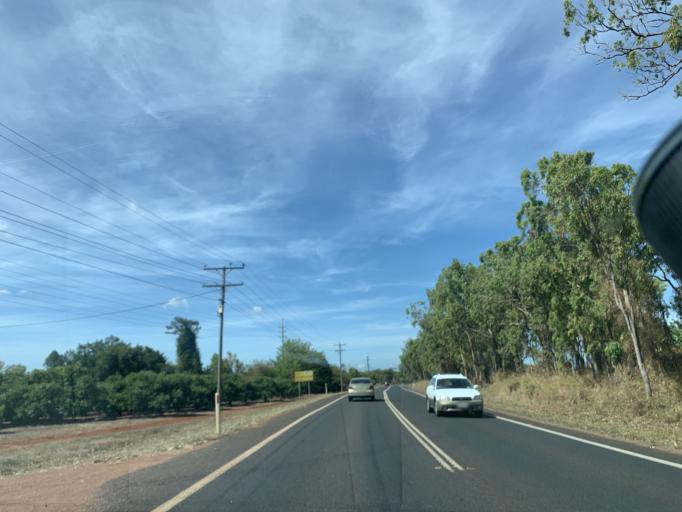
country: AU
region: Queensland
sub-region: Tablelands
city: Mareeba
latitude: -17.1116
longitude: 145.4294
